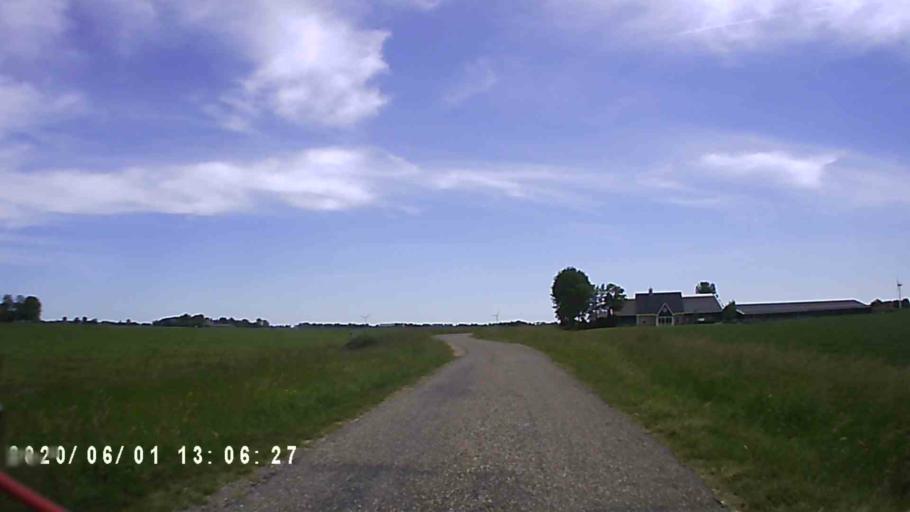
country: NL
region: Friesland
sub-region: Gemeente Franekeradeel
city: Tzum
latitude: 53.1343
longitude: 5.5512
